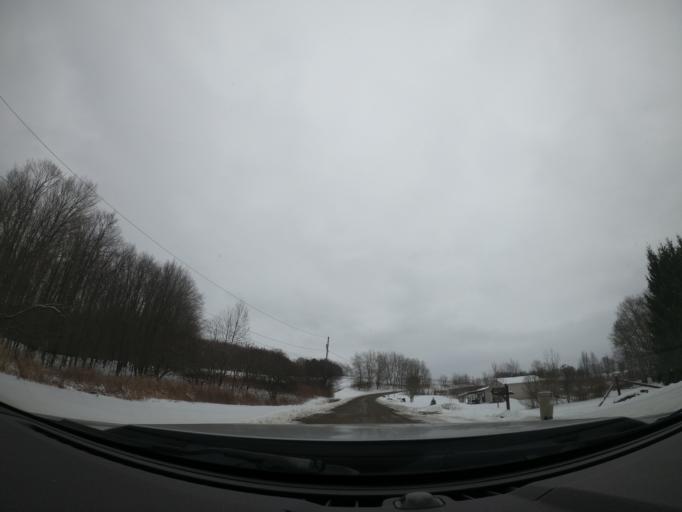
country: US
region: New York
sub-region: Cortland County
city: Homer
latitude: 42.7277
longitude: -76.2802
